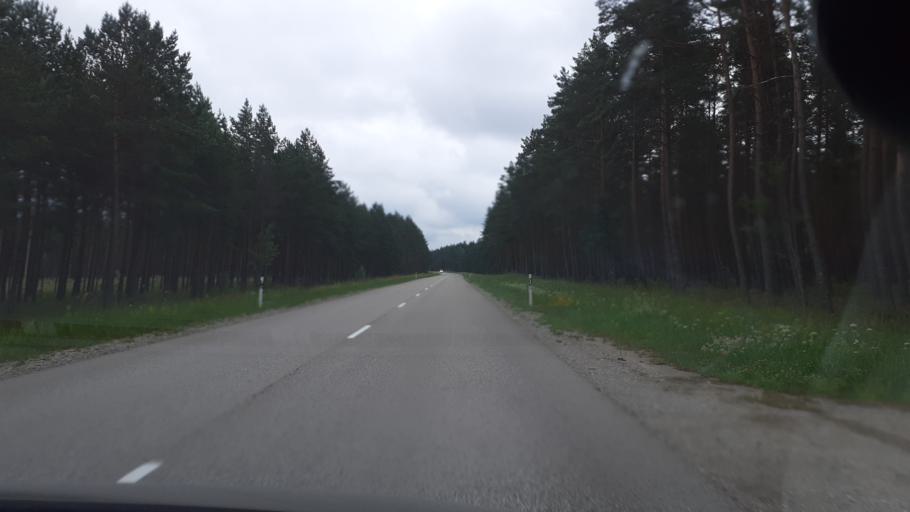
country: LV
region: Ventspils Rajons
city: Piltene
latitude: 57.1228
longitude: 21.7418
